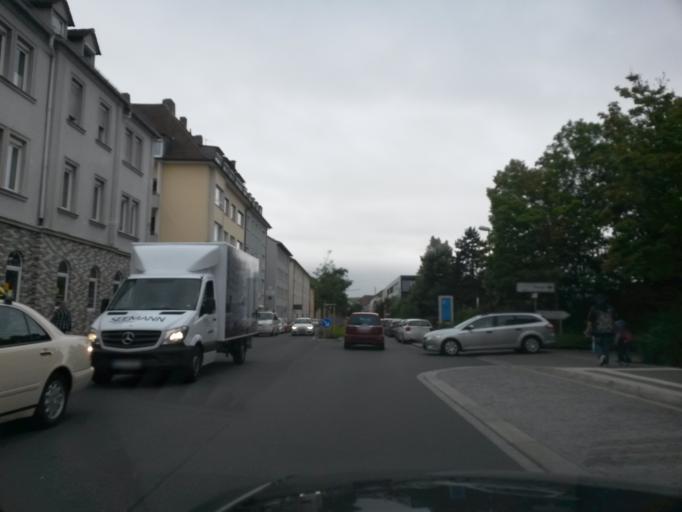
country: DE
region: Bavaria
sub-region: Regierungsbezirk Unterfranken
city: Wuerzburg
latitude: 49.7976
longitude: 9.9159
